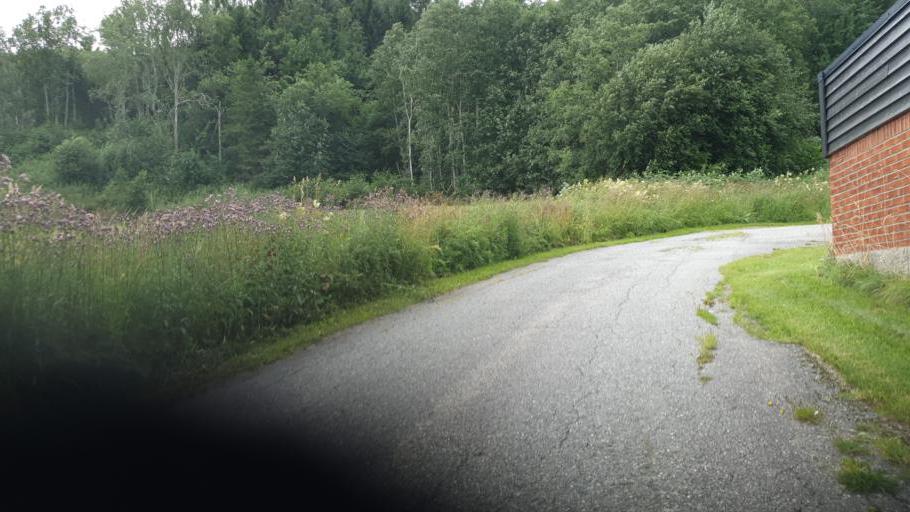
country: NO
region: Sor-Trondelag
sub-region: Malvik
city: Malvik
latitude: 63.4354
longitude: 10.6569
